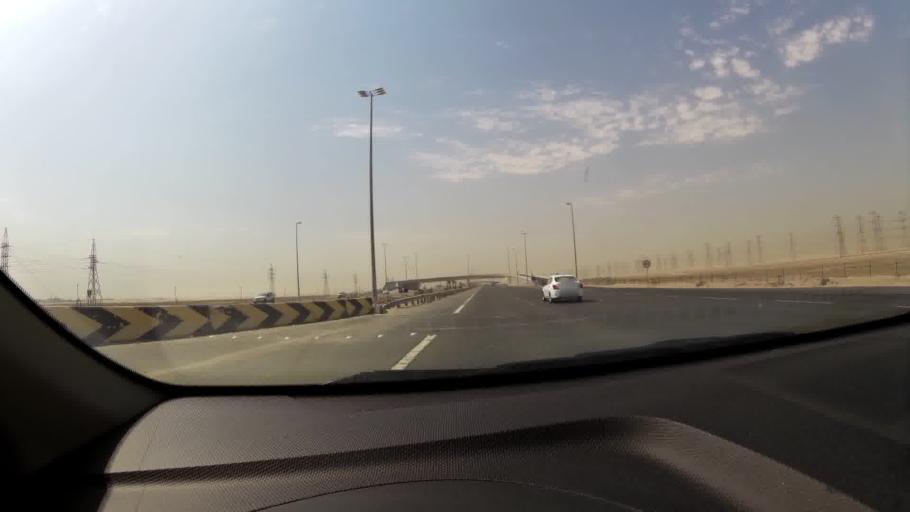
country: KW
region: Al Ahmadi
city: Al Fahahil
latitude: 28.7906
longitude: 48.2730
